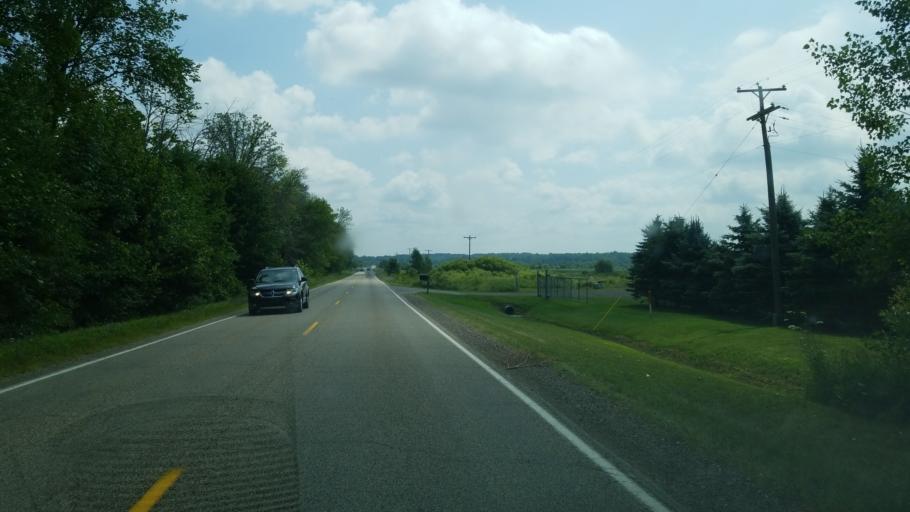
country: US
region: Michigan
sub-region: Kent County
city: Cedar Springs
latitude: 43.2202
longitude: -85.5271
